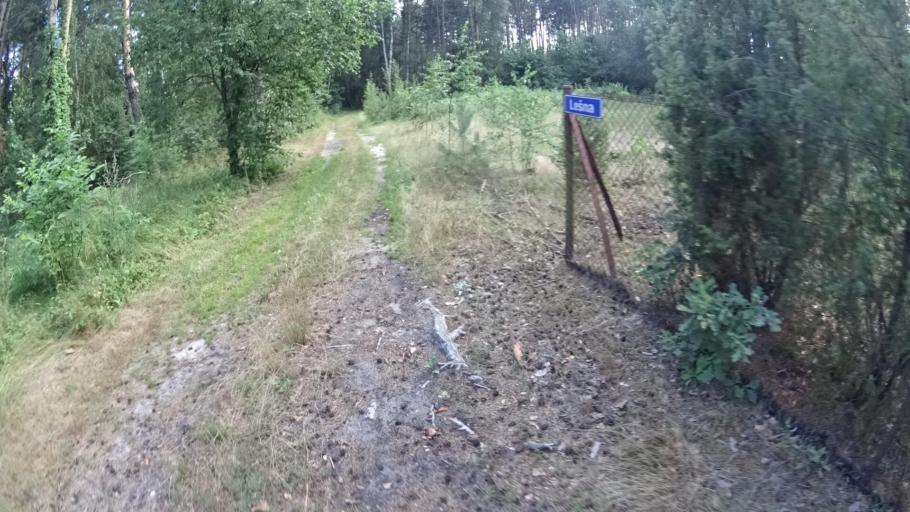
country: PL
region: Masovian Voivodeship
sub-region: Powiat piaseczynski
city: Tarczyn
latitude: 51.9712
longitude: 20.8682
